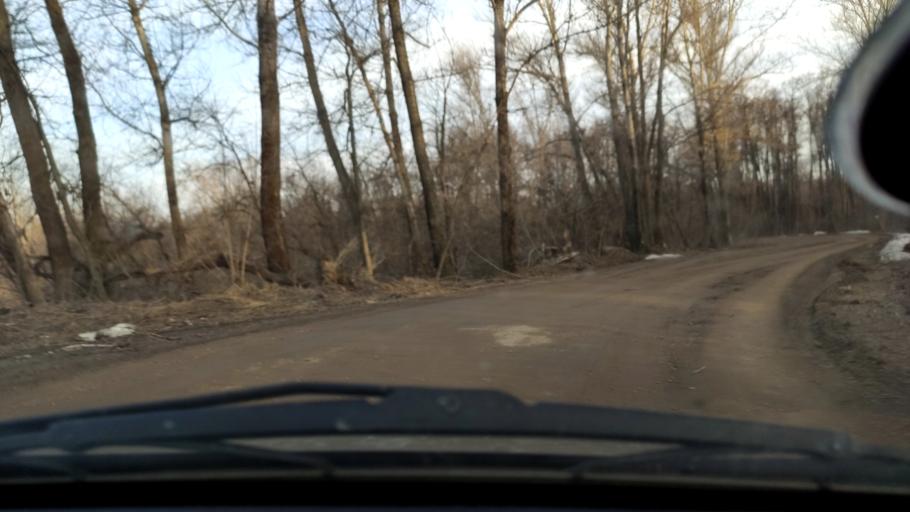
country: RU
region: Bashkortostan
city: Ufa
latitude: 54.7967
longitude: 56.1871
